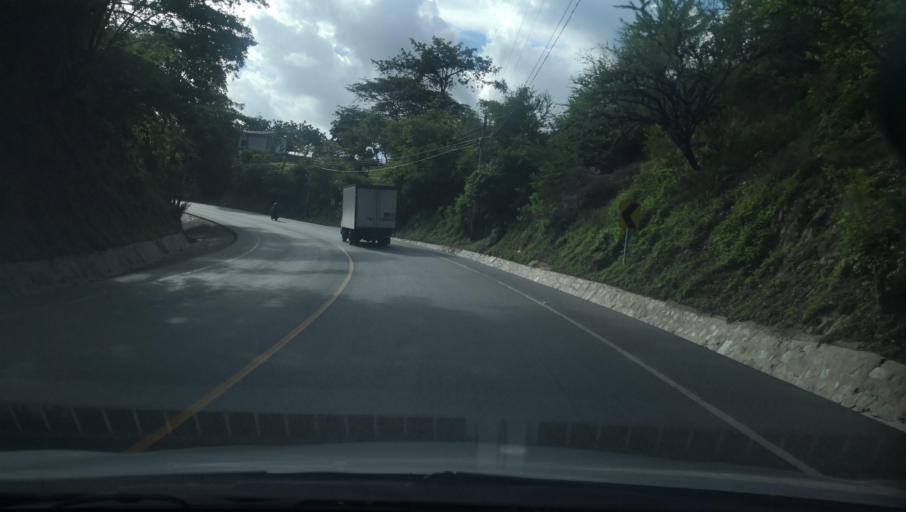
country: NI
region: Nueva Segovia
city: Ocotal
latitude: 13.6127
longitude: -86.4704
